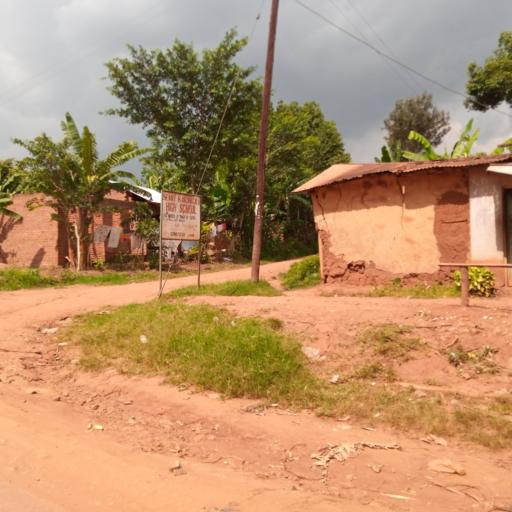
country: UG
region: Eastern Region
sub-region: Mbale District
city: Mbale
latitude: 1.1059
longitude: 34.1994
